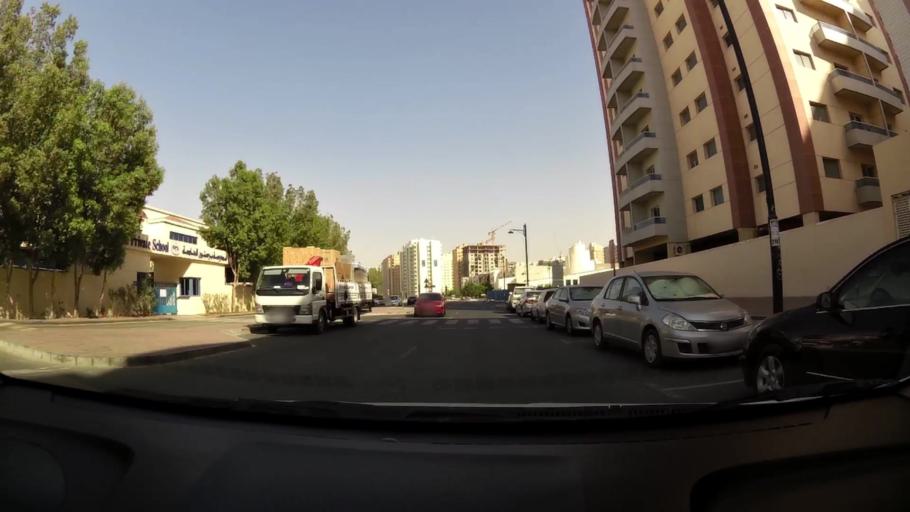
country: AE
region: Ash Shariqah
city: Sharjah
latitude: 25.2936
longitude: 55.3743
